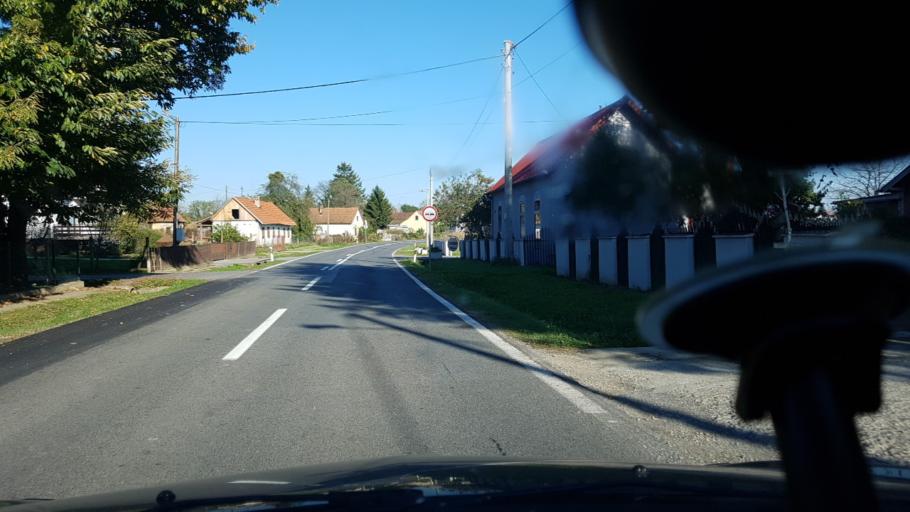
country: HR
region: Bjelovarsko-Bilogorska
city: Gudovac
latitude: 45.8349
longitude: 16.7804
